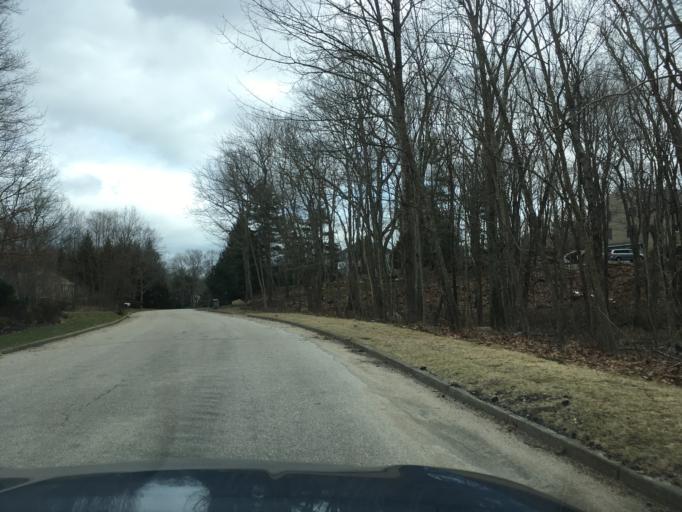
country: US
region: Rhode Island
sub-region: Kent County
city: West Warwick
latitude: 41.6546
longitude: -71.5160
